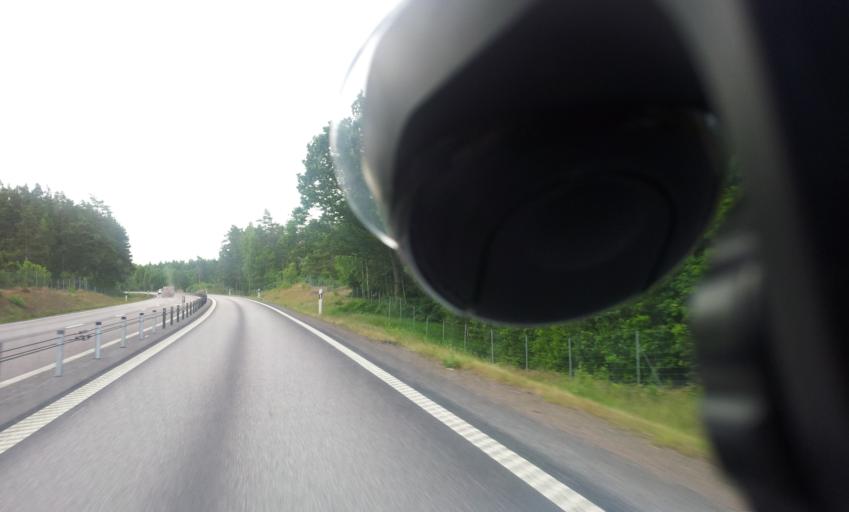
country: SE
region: Kalmar
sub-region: Oskarshamns Kommun
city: Paskallavik
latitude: 57.1621
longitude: 16.4459
